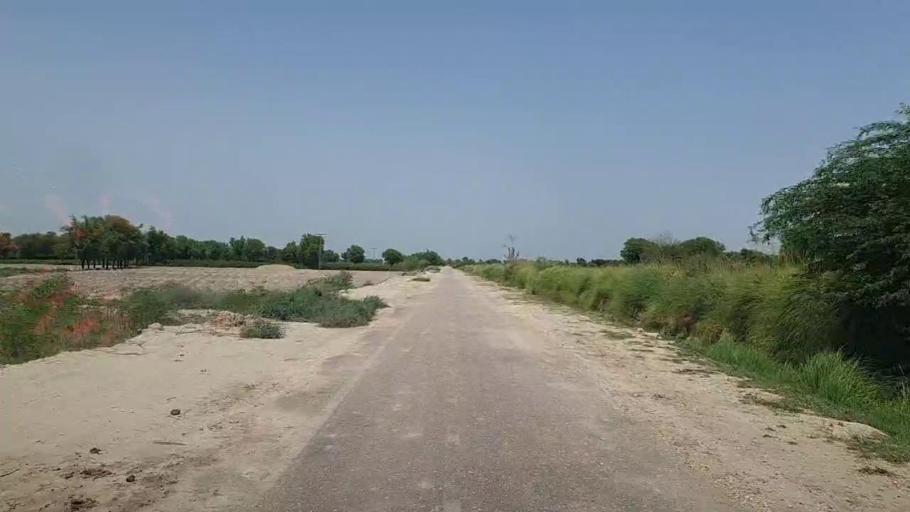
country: PK
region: Sindh
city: Pad Idan
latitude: 26.7497
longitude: 68.3156
